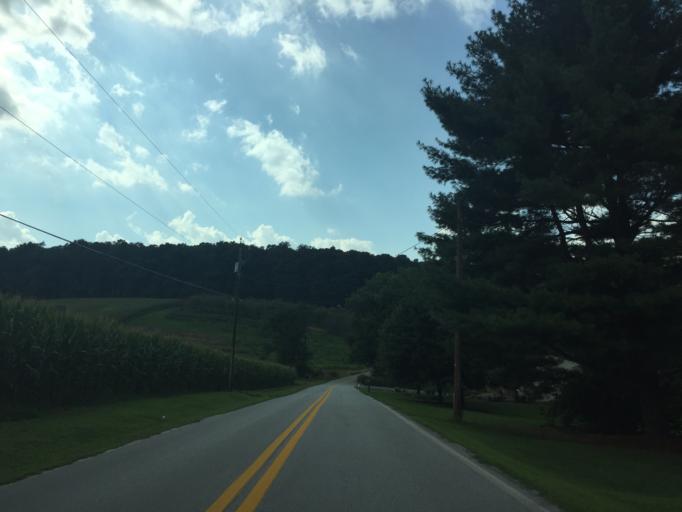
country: US
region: Maryland
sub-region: Carroll County
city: Manchester
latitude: 39.6287
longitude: -76.9053
